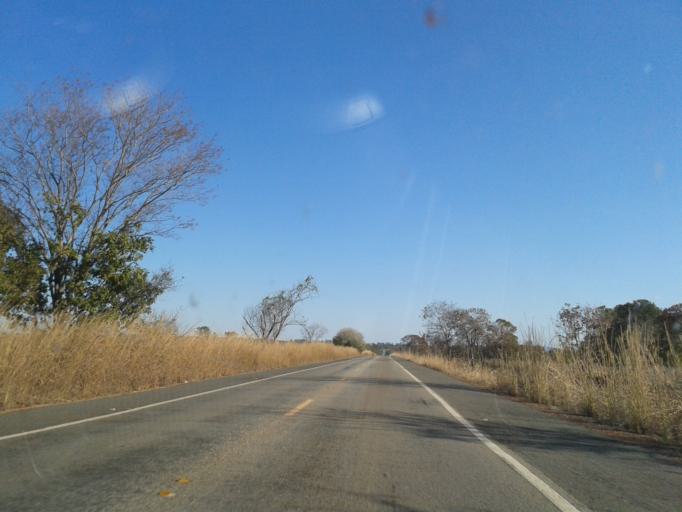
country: BR
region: Goias
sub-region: Mozarlandia
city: Mozarlandia
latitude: -15.0555
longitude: -50.6116
